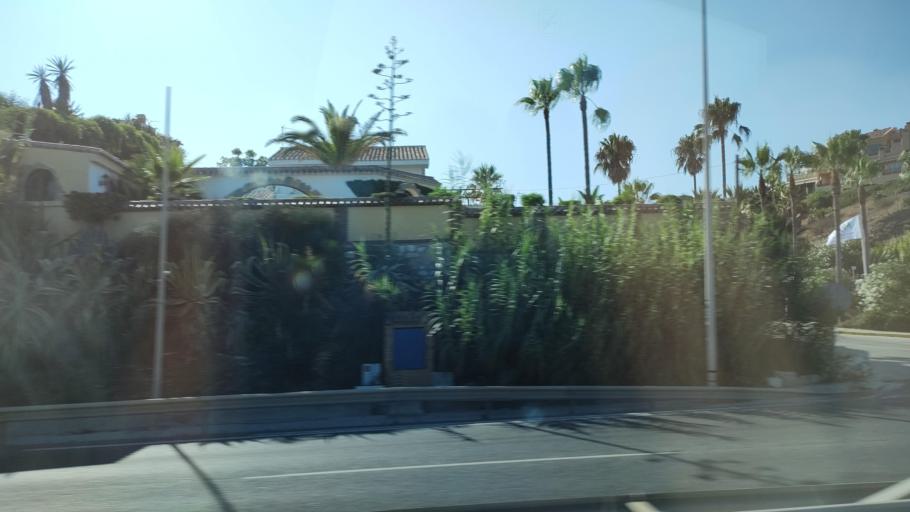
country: ES
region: Andalusia
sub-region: Provincia de Malaga
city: Fuengirola
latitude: 36.5107
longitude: -4.6360
